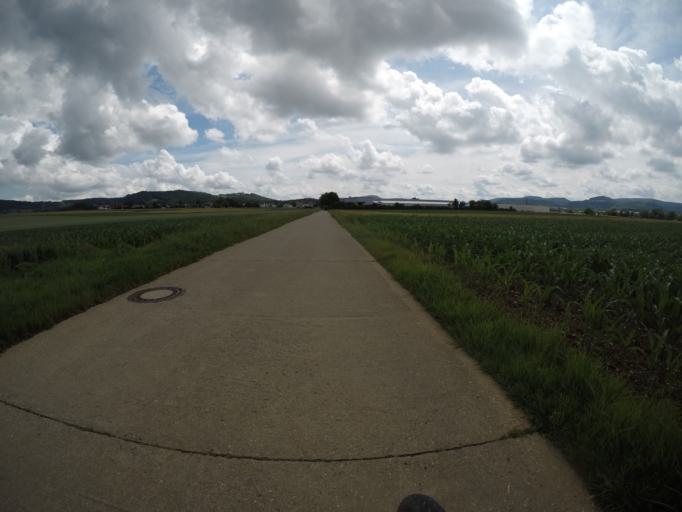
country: DE
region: Baden-Wuerttemberg
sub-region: Regierungsbezirk Stuttgart
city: Salach
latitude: 48.6972
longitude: 9.7277
